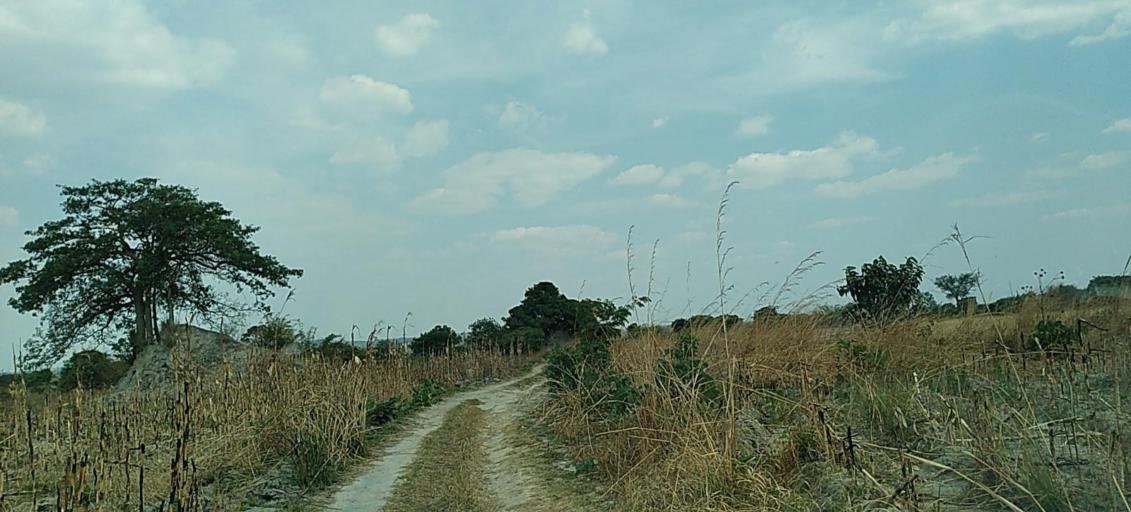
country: ZM
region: Copperbelt
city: Chililabombwe
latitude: -12.3451
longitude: 27.7907
